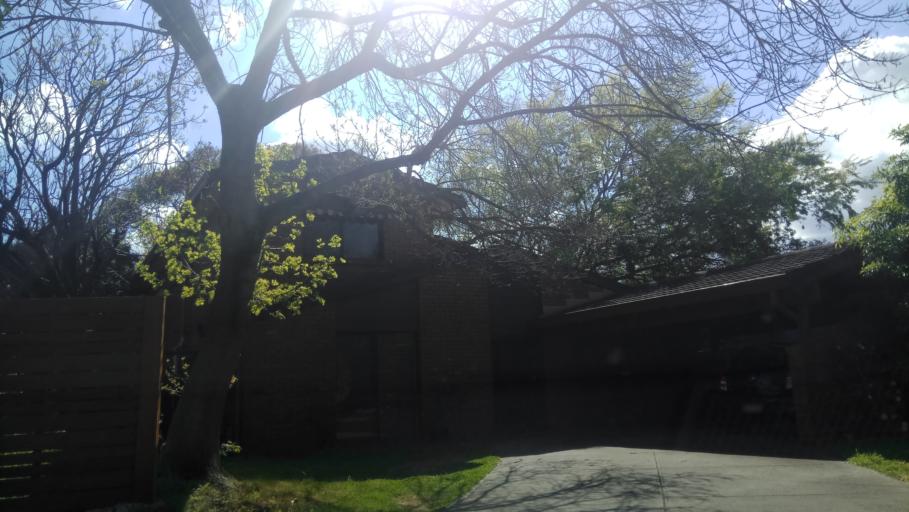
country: AU
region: Victoria
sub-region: Kingston
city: Dingley Village
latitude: -37.9819
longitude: 145.1251
